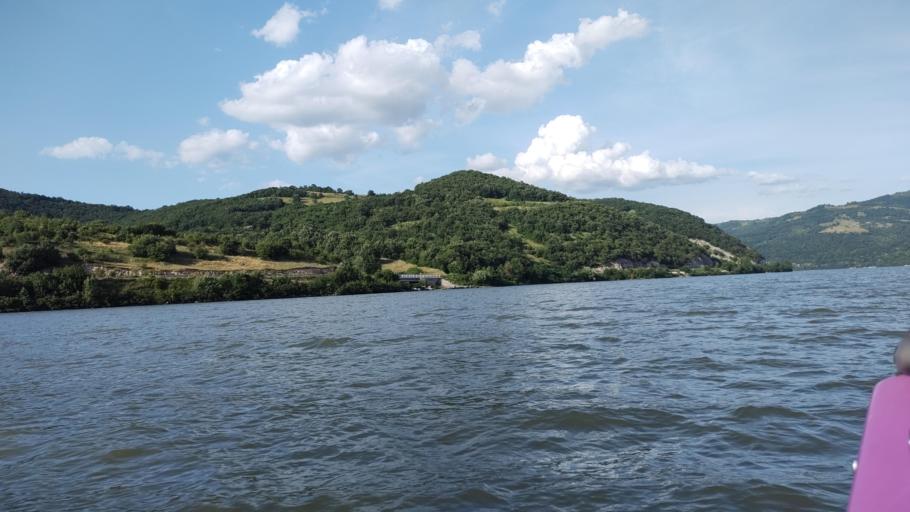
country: RO
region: Mehedinti
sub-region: Comuna Svinita
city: Svinita
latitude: 44.4793
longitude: 22.1577
